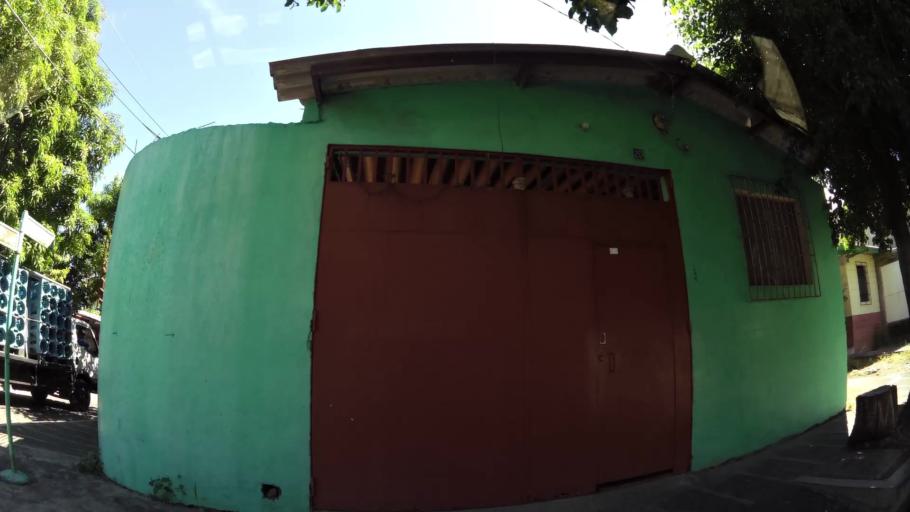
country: SV
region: San Miguel
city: San Miguel
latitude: 13.4809
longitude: -88.1672
